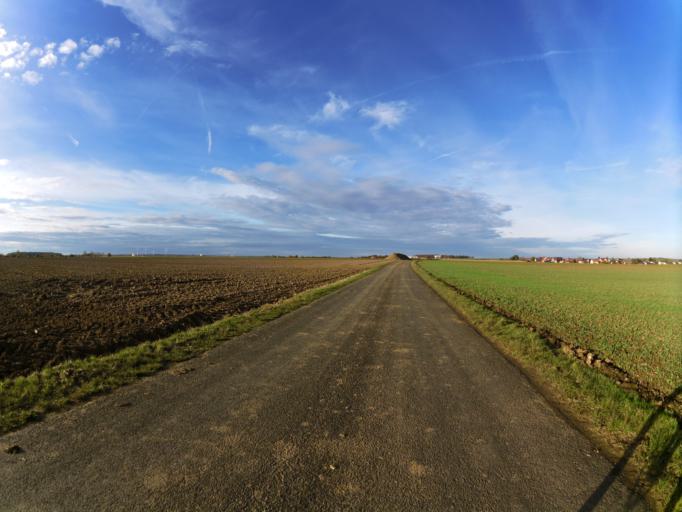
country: DE
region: Bavaria
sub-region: Regierungsbezirk Unterfranken
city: Giebelstadt
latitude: 49.6642
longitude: 9.9516
